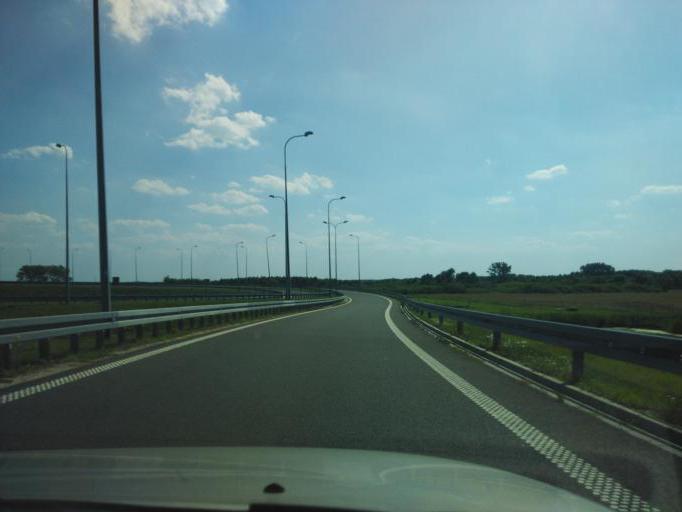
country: PL
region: West Pomeranian Voivodeship
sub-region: Powiat pyrzycki
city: Bielice
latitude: 53.1249
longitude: 14.7357
